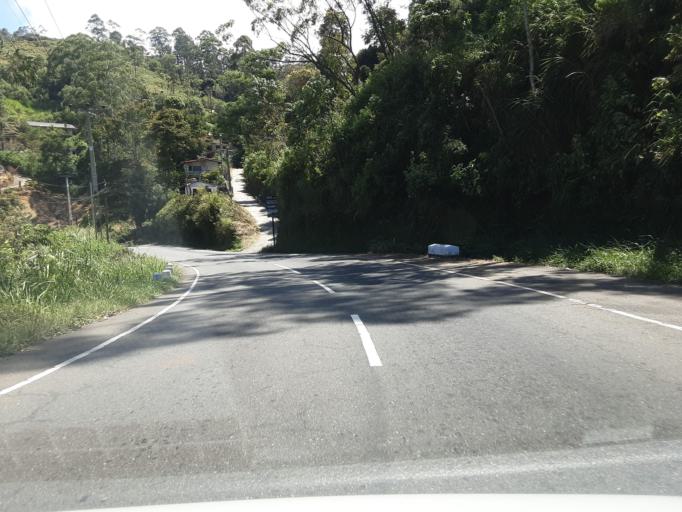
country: LK
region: Uva
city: Haputale
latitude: 6.7654
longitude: 80.9538
